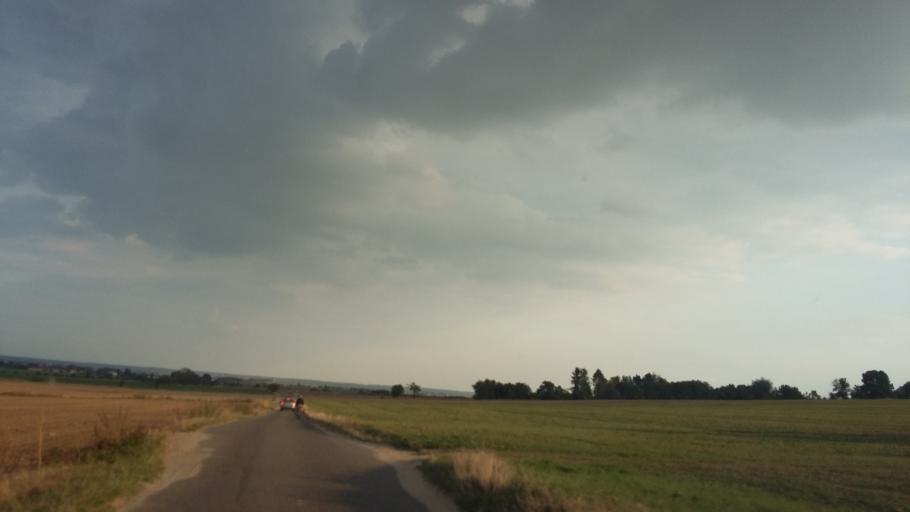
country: CZ
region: Central Bohemia
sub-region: Okres Mlada Boleslav
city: Mlada Boleslav
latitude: 50.3600
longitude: 14.8885
